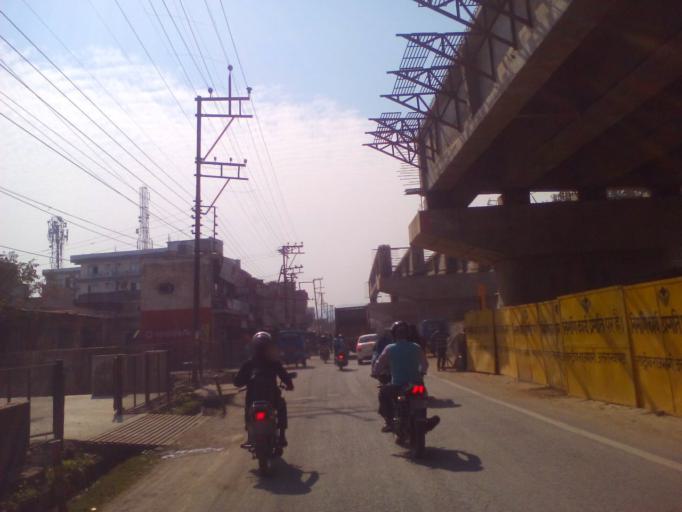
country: IN
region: Uttarakhand
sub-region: Dehradun
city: Clement Town
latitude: 30.2871
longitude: 77.9961
